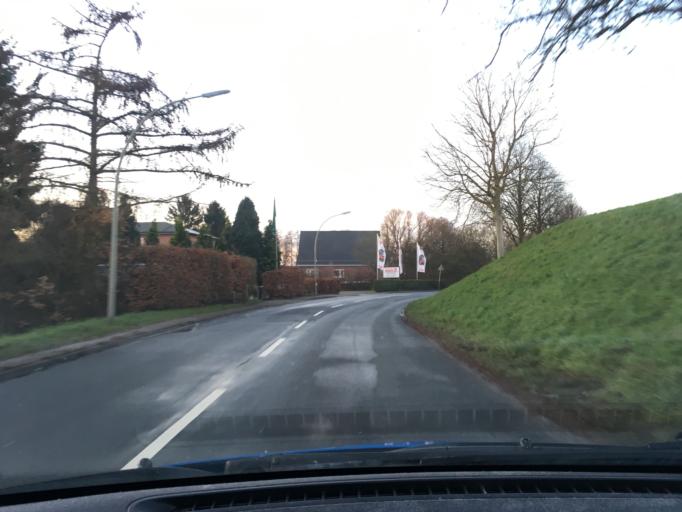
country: DE
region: Hamburg
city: Altona
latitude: 53.5011
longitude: 9.8806
